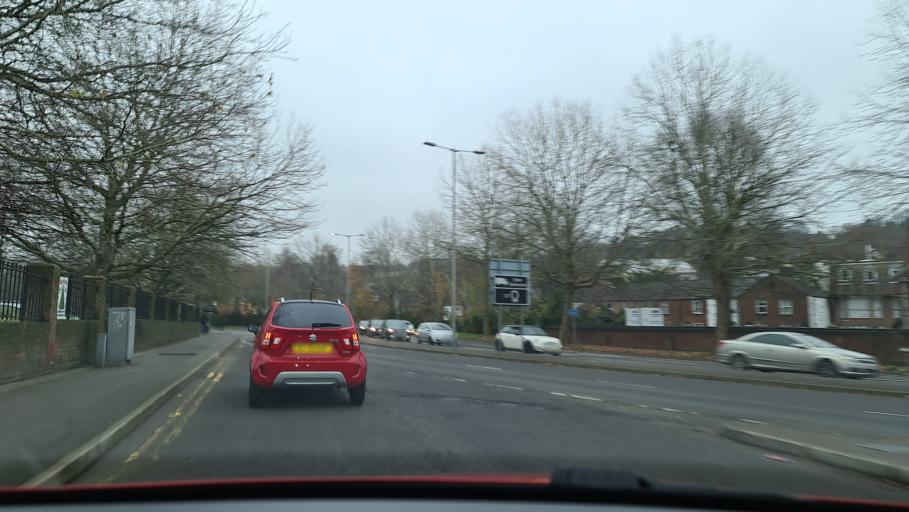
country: GB
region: England
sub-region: Buckinghamshire
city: High Wycombe
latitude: 51.6335
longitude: -0.7532
